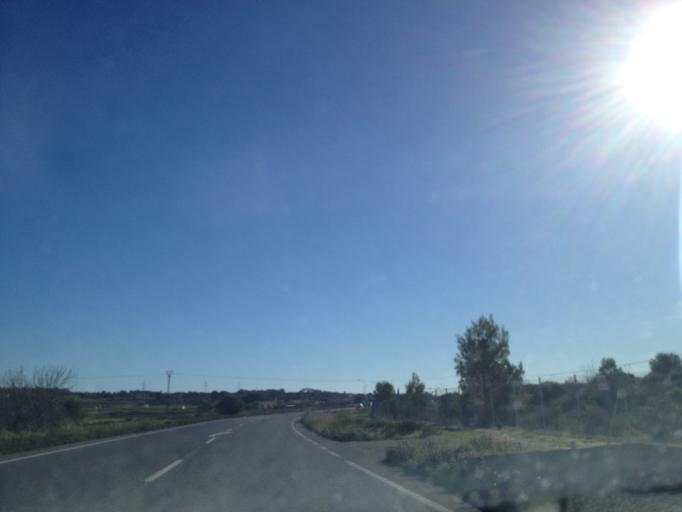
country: ES
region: Balearic Islands
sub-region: Illes Balears
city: Petra
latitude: 39.6192
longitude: 3.1184
